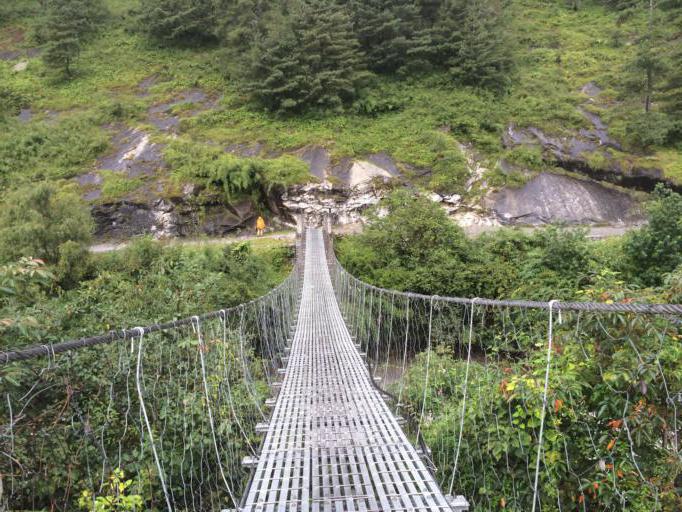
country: NP
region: Western Region
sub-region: Dhawalagiri Zone
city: Jomsom
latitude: 28.6469
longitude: 83.5947
